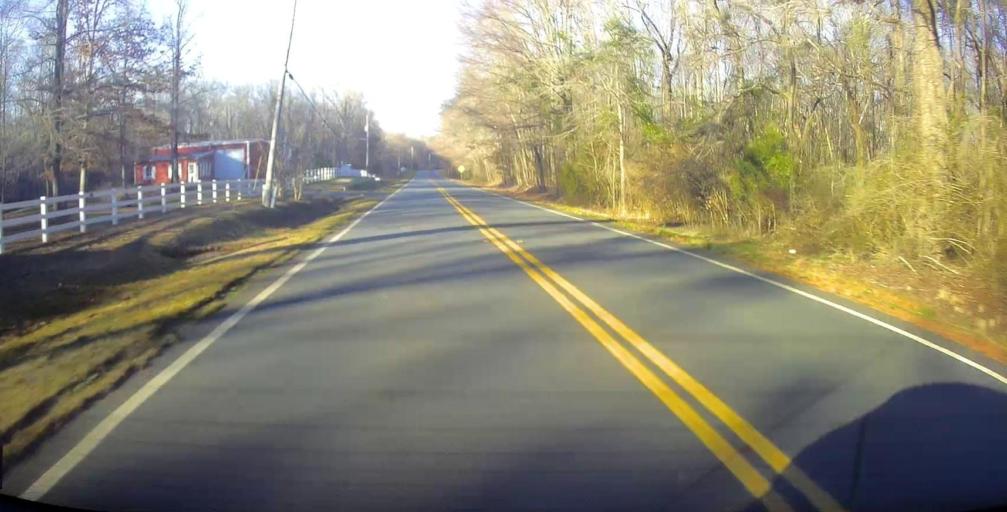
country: US
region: Georgia
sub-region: Harris County
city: Pine Mountain
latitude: 32.9102
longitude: -84.8022
